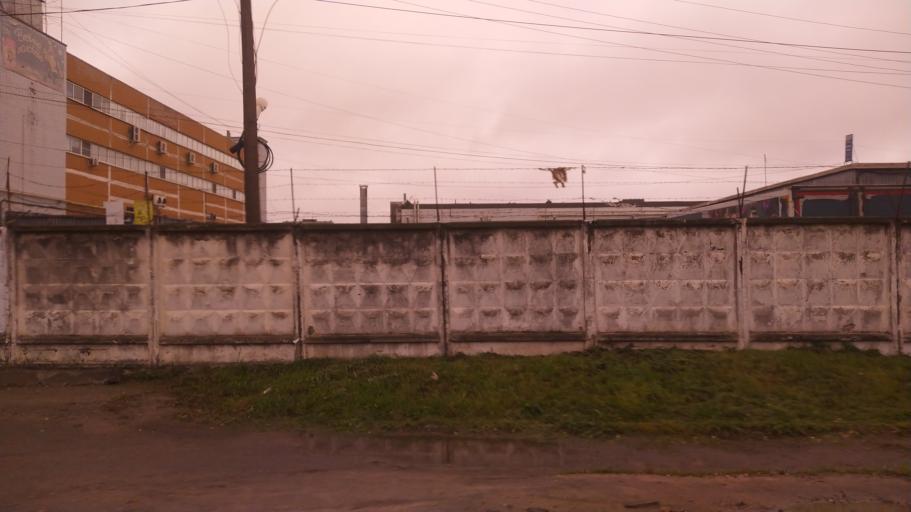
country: RU
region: Tverskaya
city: Tver
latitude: 56.8305
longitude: 35.9099
